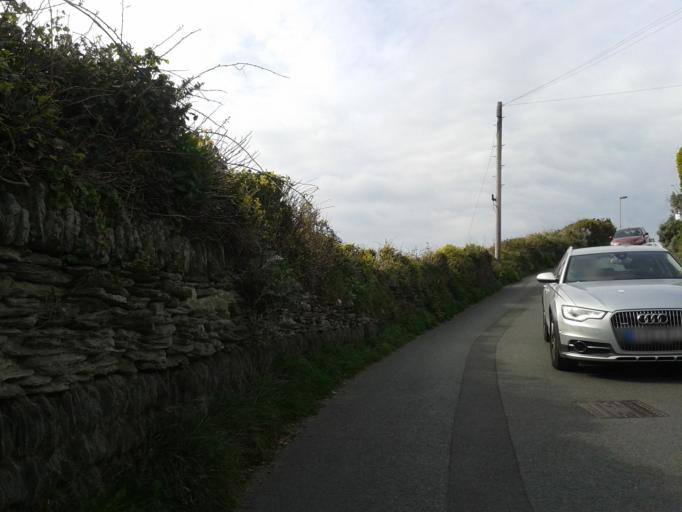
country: GB
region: England
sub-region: Devon
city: Braunton
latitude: 51.1793
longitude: -4.2116
